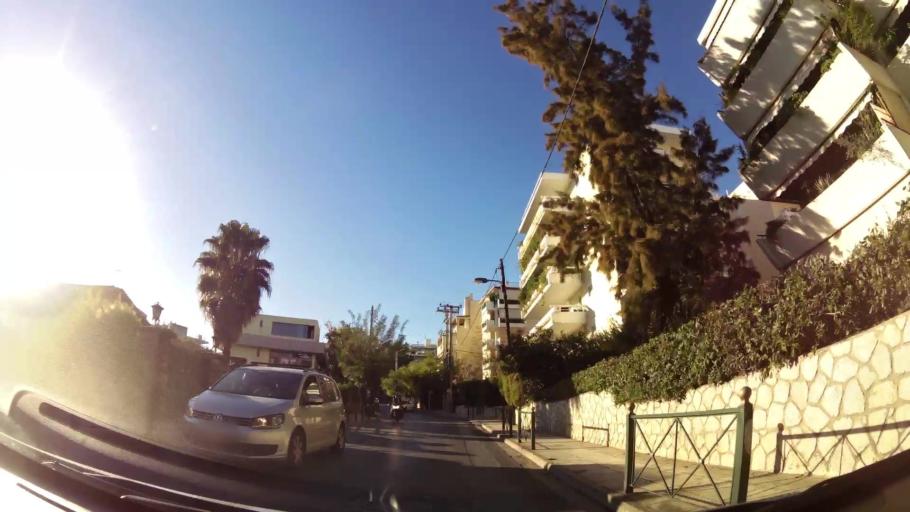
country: GR
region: Attica
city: Pefki
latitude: 38.0584
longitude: 23.8006
